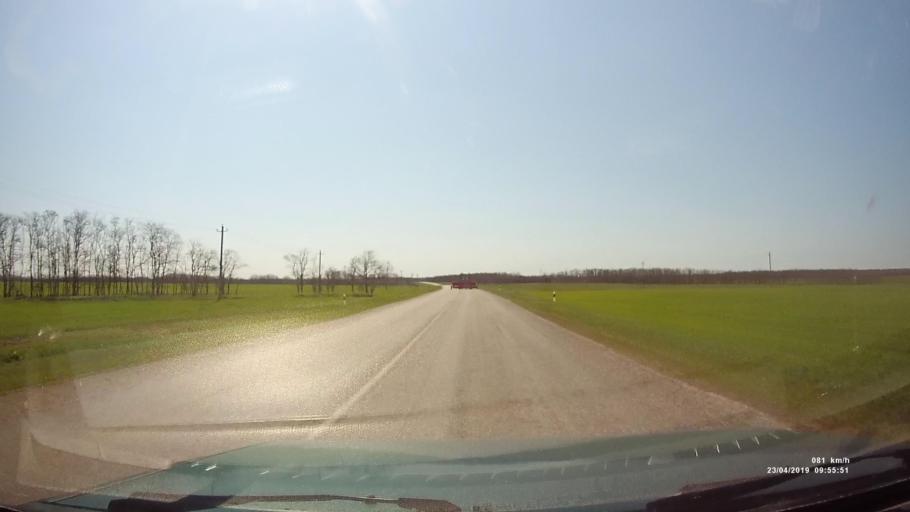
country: RU
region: Rostov
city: Orlovskiy
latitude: 46.8039
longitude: 42.0660
